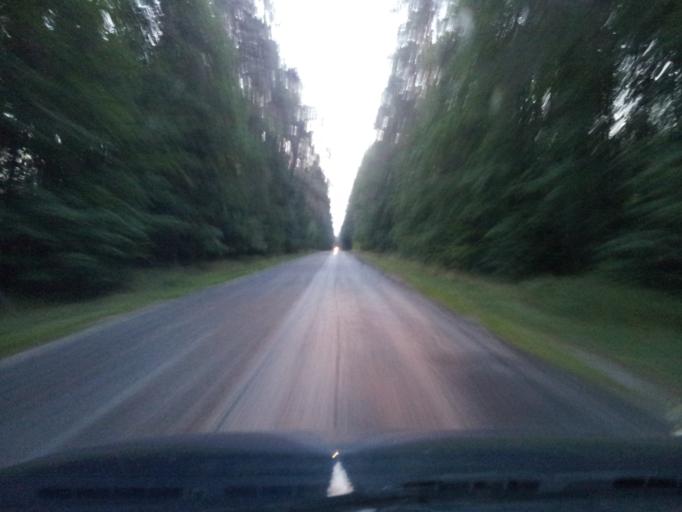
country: PL
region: Kujawsko-Pomorskie
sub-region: Powiat wabrzeski
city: Debowa Laka
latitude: 53.1833
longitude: 19.1472
